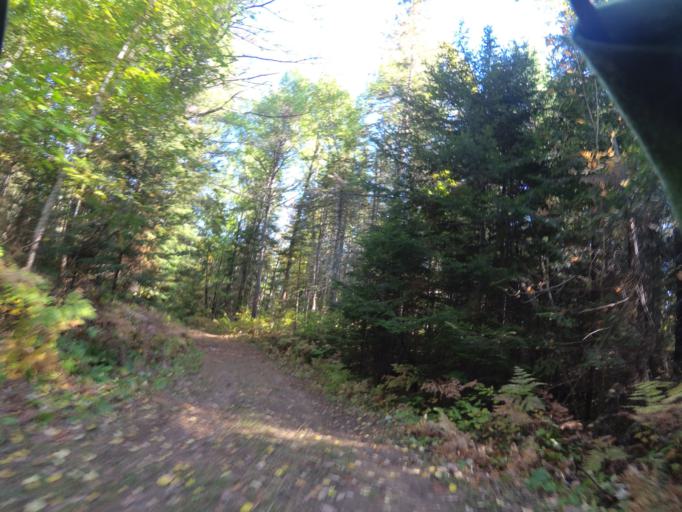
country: CA
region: Ontario
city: Pembroke
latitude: 45.3454
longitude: -77.1748
